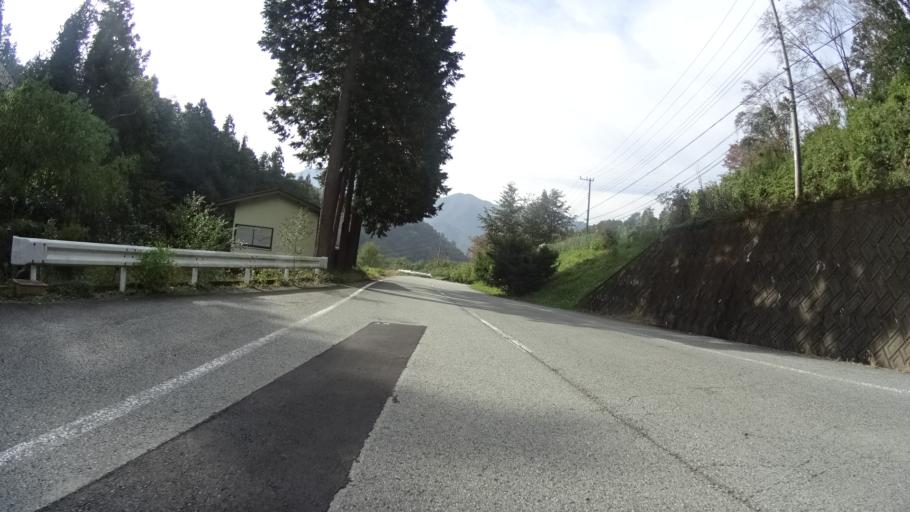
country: JP
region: Yamanashi
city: Otsuki
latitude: 35.6190
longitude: 139.0177
